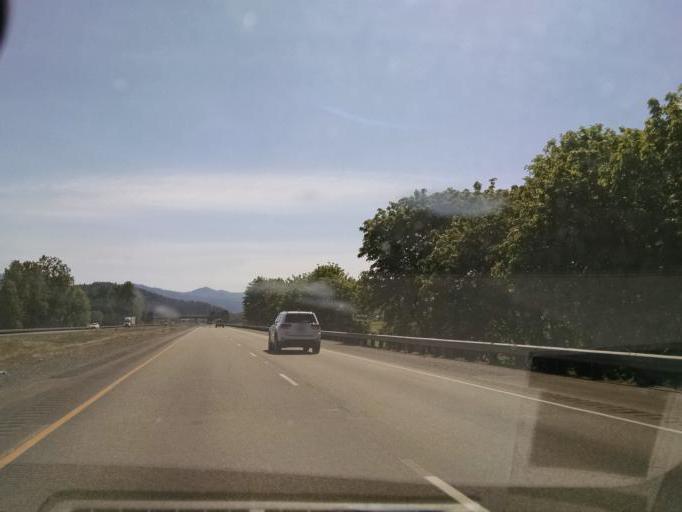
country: US
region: Oregon
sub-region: Douglas County
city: Tri-City
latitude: 42.9917
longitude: -123.3267
